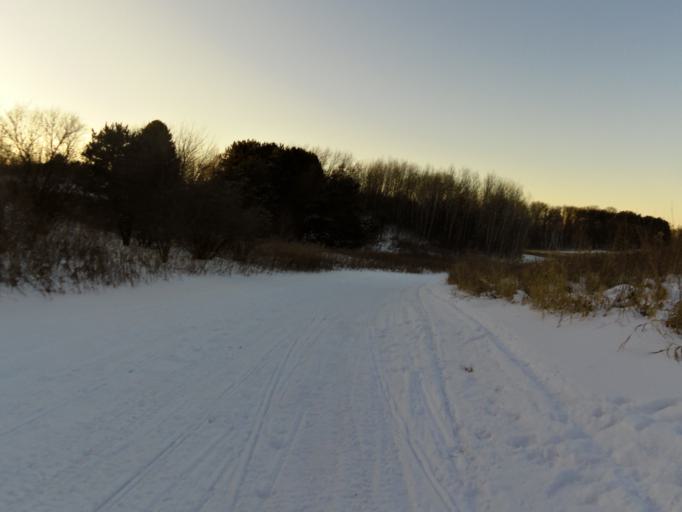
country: US
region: Minnesota
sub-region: Washington County
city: Oakdale
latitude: 44.9730
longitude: -92.9214
